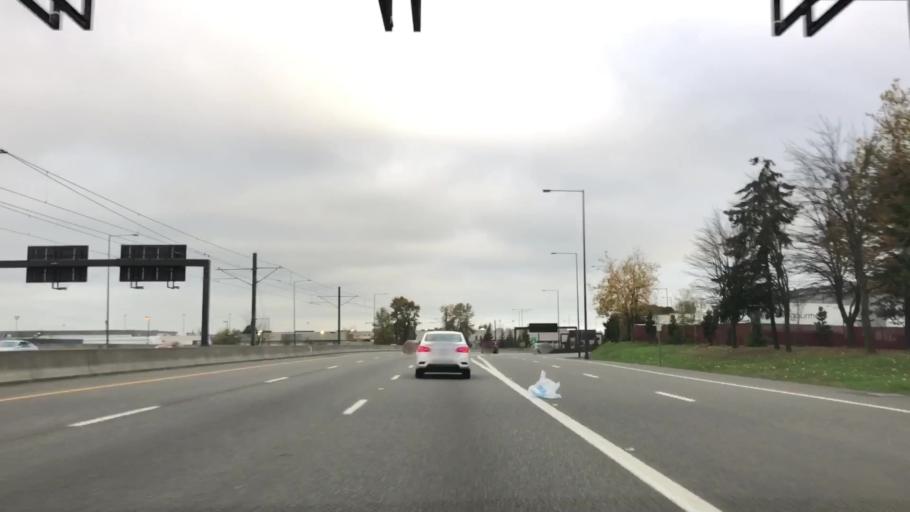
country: US
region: Washington
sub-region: King County
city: SeaTac
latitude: 47.4556
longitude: -122.3003
